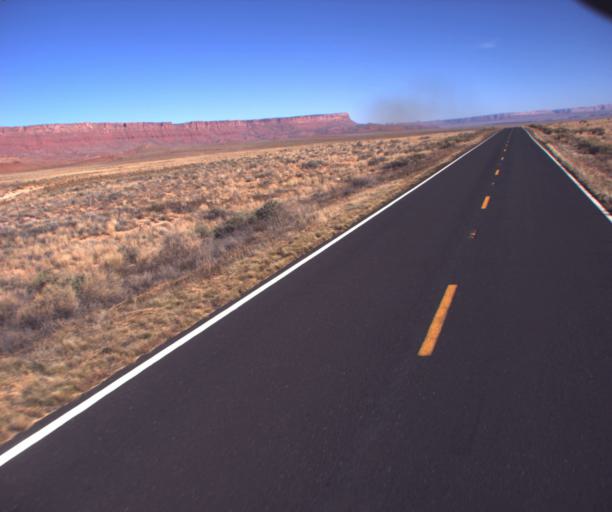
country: US
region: Arizona
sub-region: Coconino County
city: Fredonia
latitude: 36.7263
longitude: -112.0301
